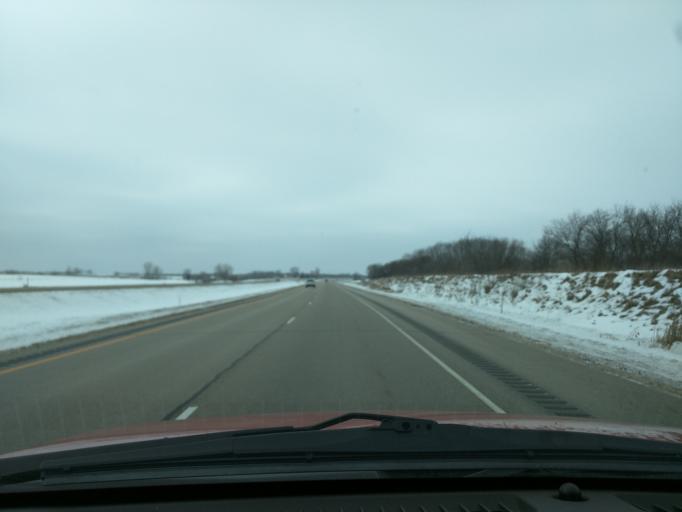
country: US
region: Wisconsin
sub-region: Trempealeau County
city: Trempealeau
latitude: 43.9165
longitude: -91.5107
